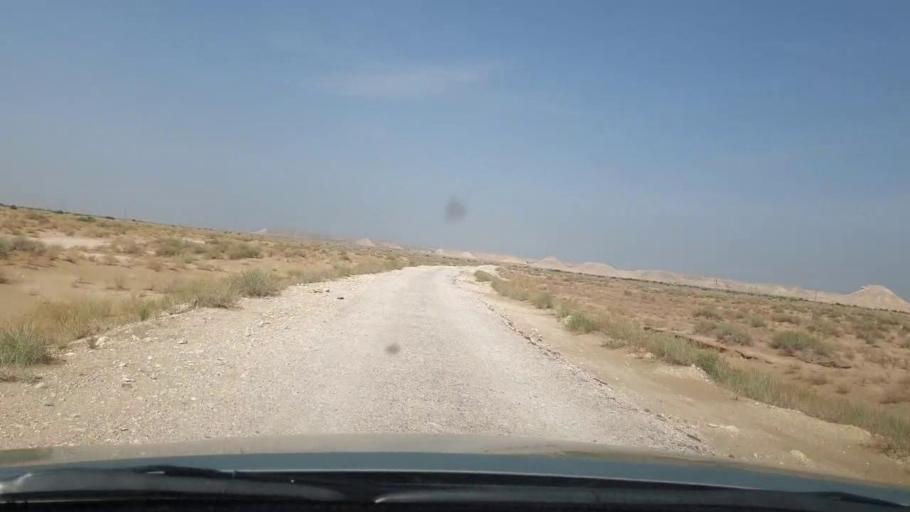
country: PK
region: Sindh
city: Kot Diji
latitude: 27.3273
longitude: 68.8060
